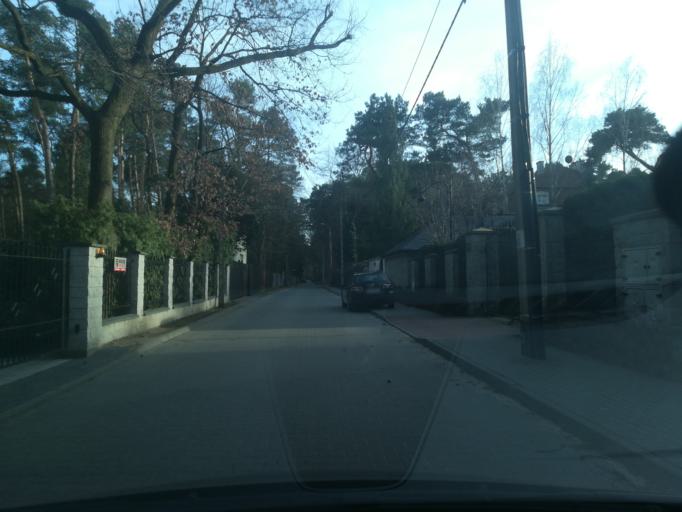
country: PL
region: Masovian Voivodeship
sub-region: Powiat piaseczynski
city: Konstancin-Jeziorna
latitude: 52.0786
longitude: 21.1071
